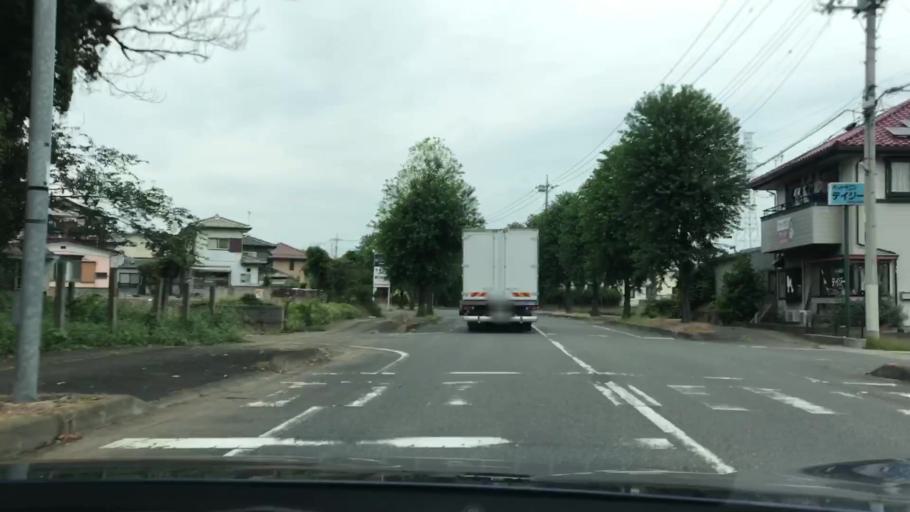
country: JP
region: Gunma
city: Isesaki
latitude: 36.3331
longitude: 139.1572
